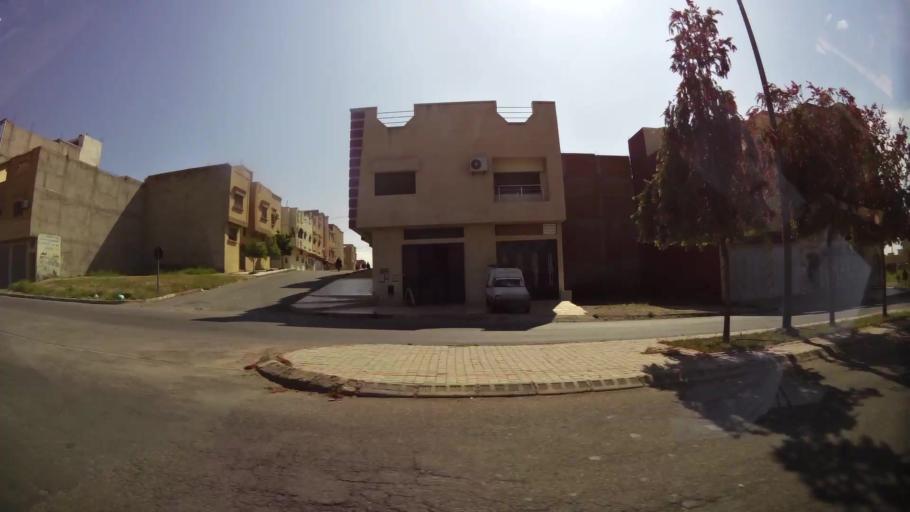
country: MA
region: Oriental
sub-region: Oujda-Angad
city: Oujda
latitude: 34.6915
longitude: -1.8788
